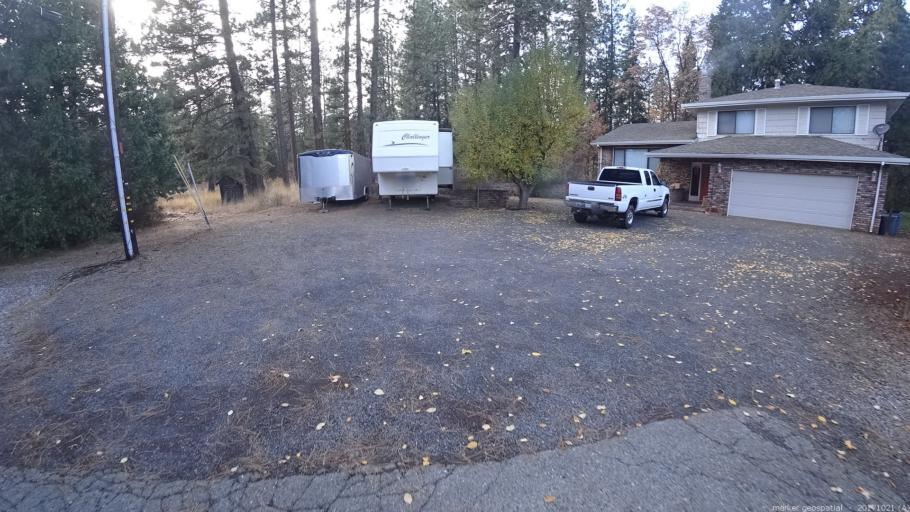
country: US
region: California
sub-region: Shasta County
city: Burney
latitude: 40.8789
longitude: -121.6662
